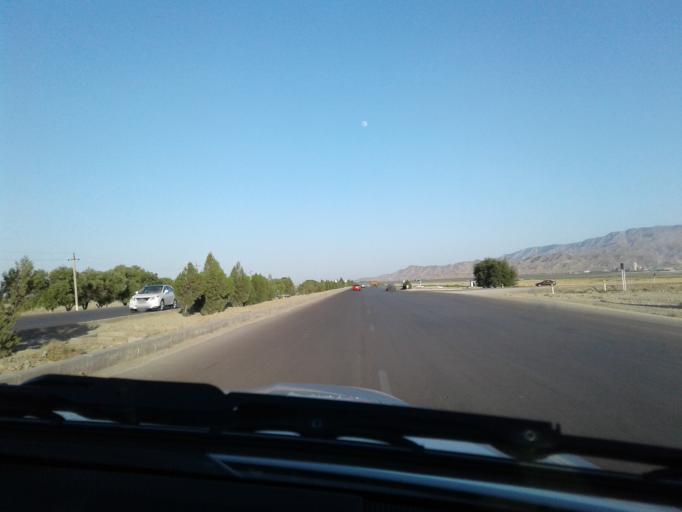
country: TM
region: Ahal
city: Baharly
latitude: 38.3046
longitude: 57.6242
